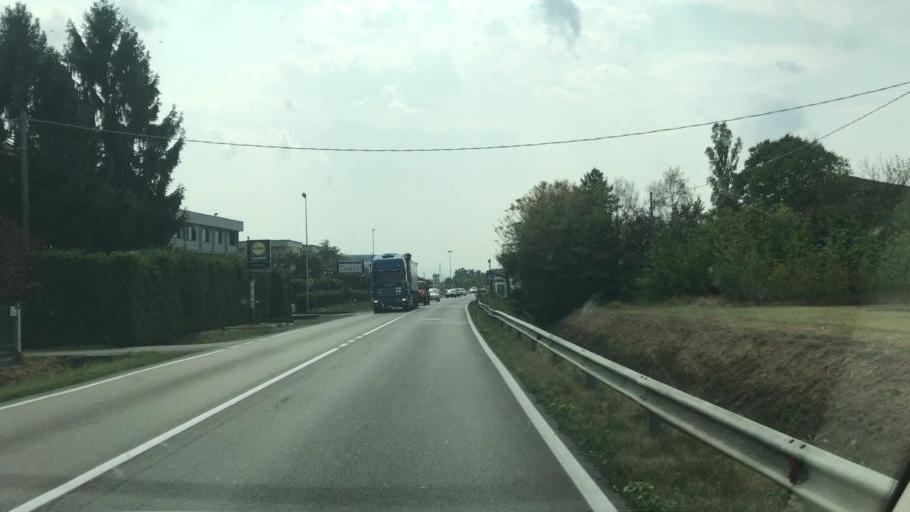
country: IT
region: Emilia-Romagna
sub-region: Provincia di Parma
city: Baganzola
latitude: 44.8529
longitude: 10.3424
